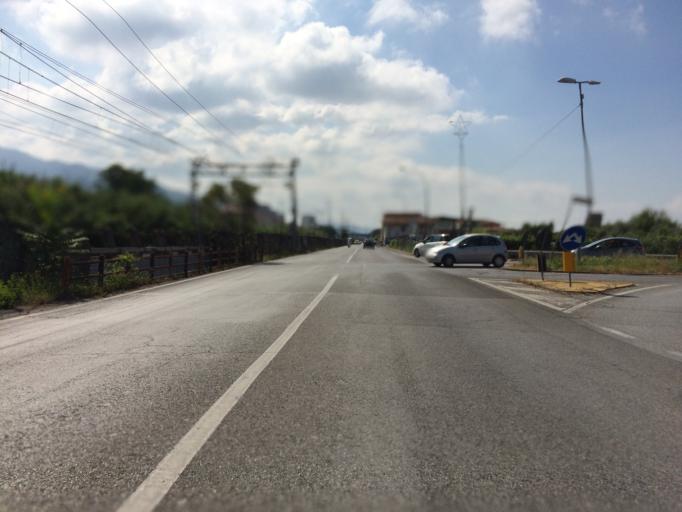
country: IT
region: Tuscany
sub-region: Provincia di Lucca
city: Strettoia
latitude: 43.9841
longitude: 10.1905
